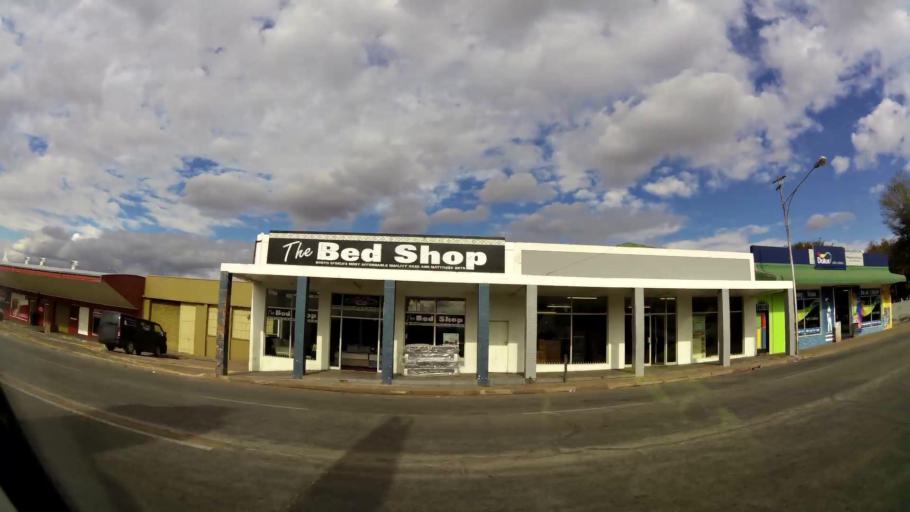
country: ZA
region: Limpopo
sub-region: Waterberg District Municipality
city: Modimolle
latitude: -24.7004
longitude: 28.4054
